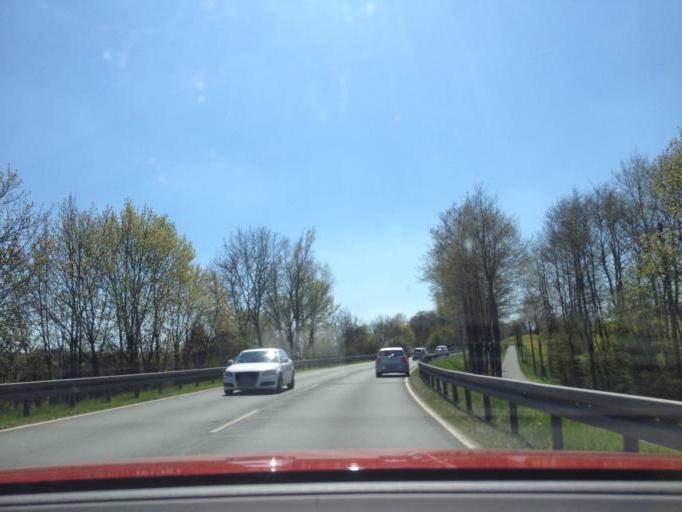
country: DE
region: Bavaria
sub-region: Upper Franconia
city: Oberkotzau
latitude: 50.2515
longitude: 11.9383
